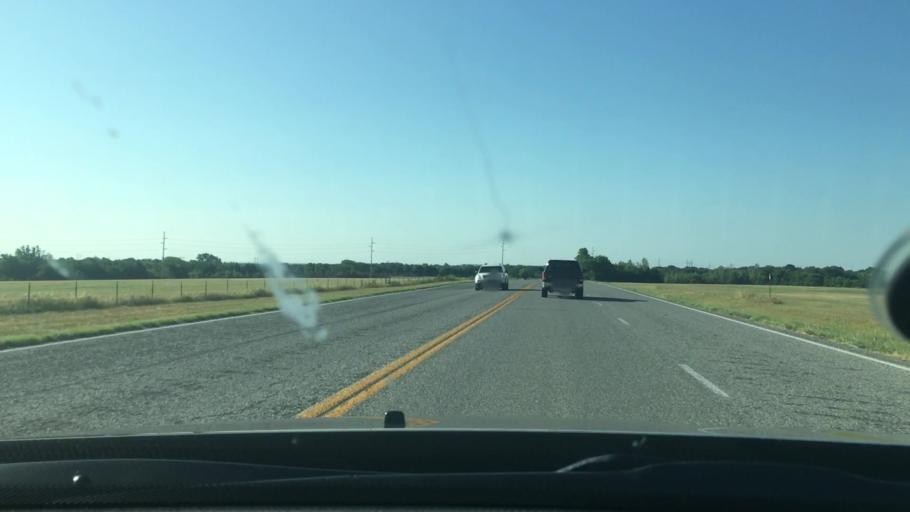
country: US
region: Oklahoma
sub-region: Johnston County
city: Tishomingo
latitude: 34.2785
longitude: -96.7790
